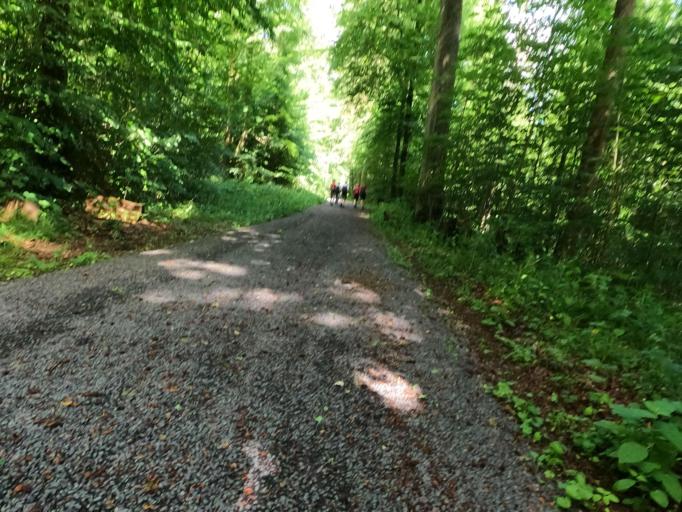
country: DE
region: Rheinland-Pfalz
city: Muschenbach
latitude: 50.6805
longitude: 7.8022
